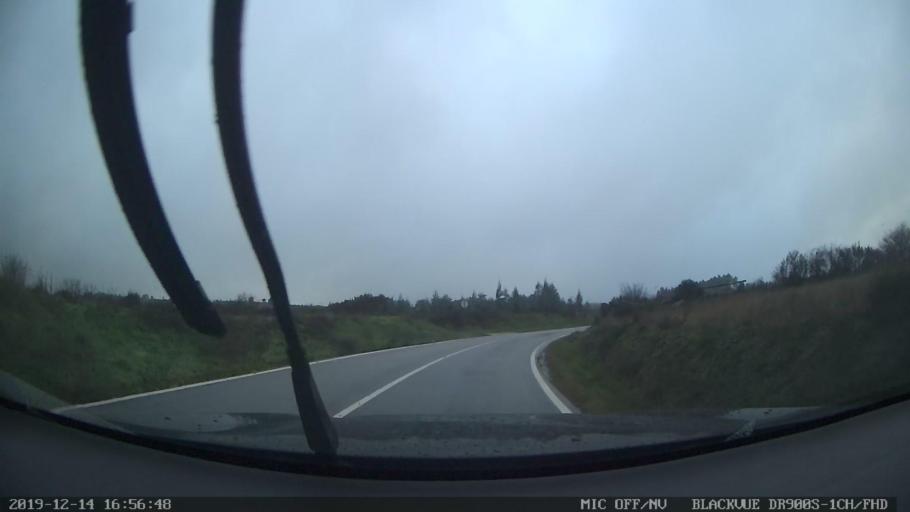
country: PT
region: Vila Real
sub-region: Murca
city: Murca
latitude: 41.4326
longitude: -7.5426
